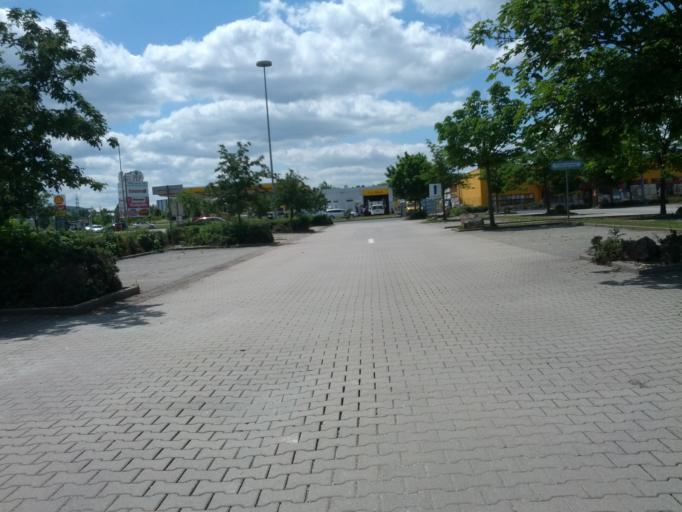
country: DE
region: Thuringia
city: Eisenach
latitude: 50.9970
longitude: 10.3553
